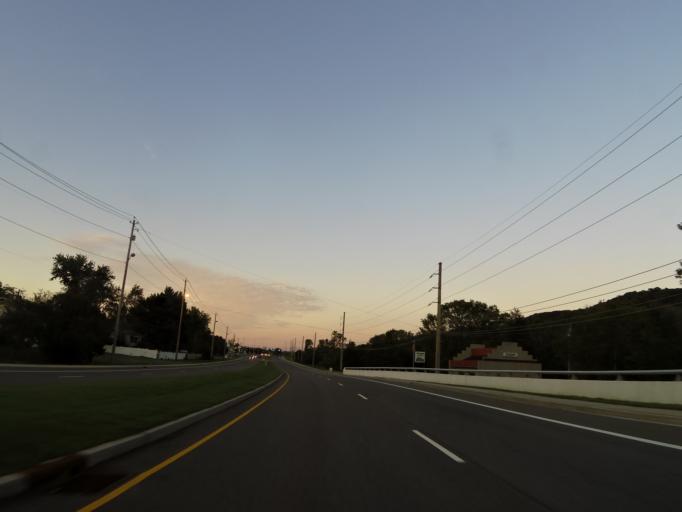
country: US
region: Tennessee
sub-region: Anderson County
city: Oak Ridge
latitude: 36.0007
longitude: -84.2928
